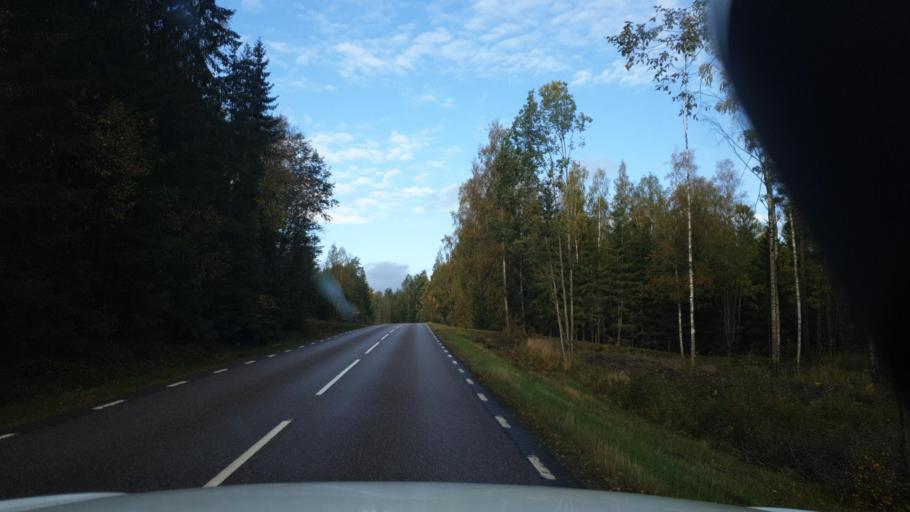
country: SE
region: Vaermland
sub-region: Arvika Kommun
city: Arvika
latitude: 59.4657
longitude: 12.7396
